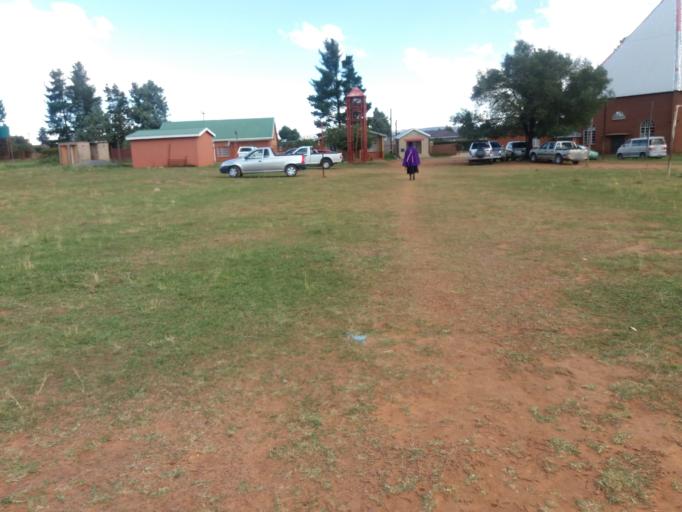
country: LS
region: Maseru
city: Maseru
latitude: -29.3713
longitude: 27.5066
